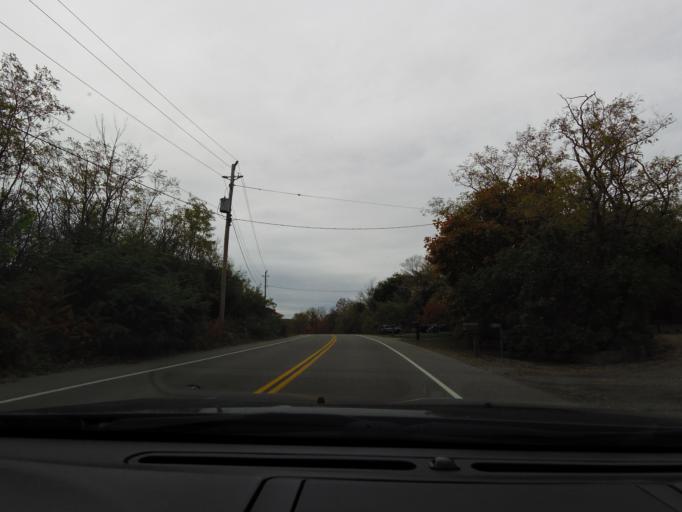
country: CA
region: Ontario
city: Hamilton
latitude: 43.3001
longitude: -79.8848
